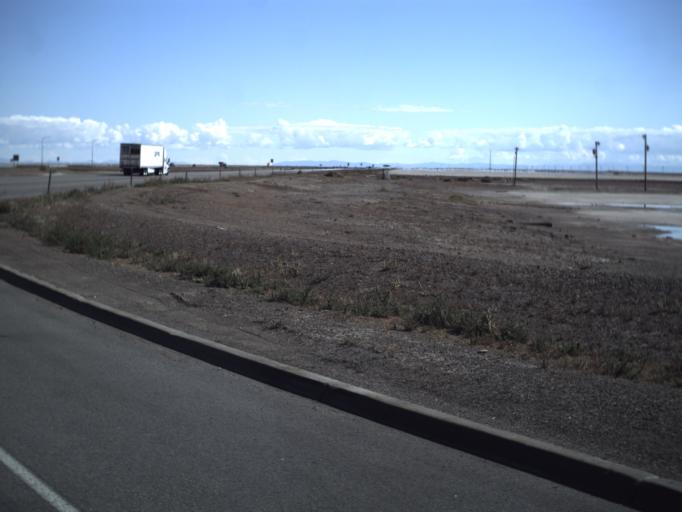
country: US
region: Utah
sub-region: Tooele County
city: Wendover
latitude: 40.7382
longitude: -113.8557
